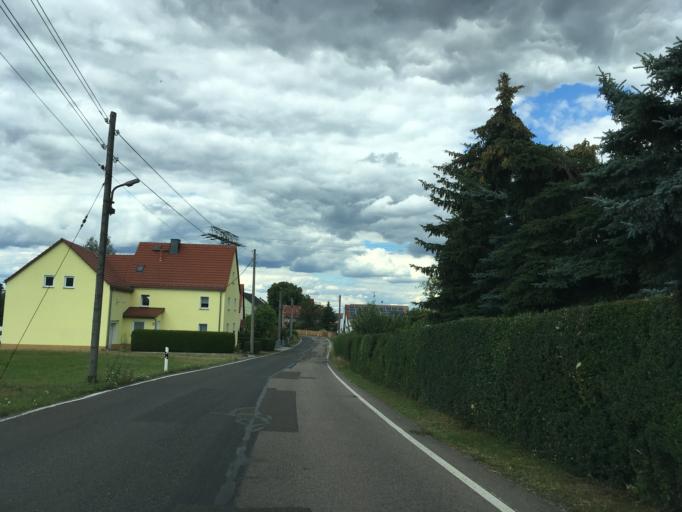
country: DE
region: Saxony
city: Wachau
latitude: 51.1493
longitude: 13.9118
